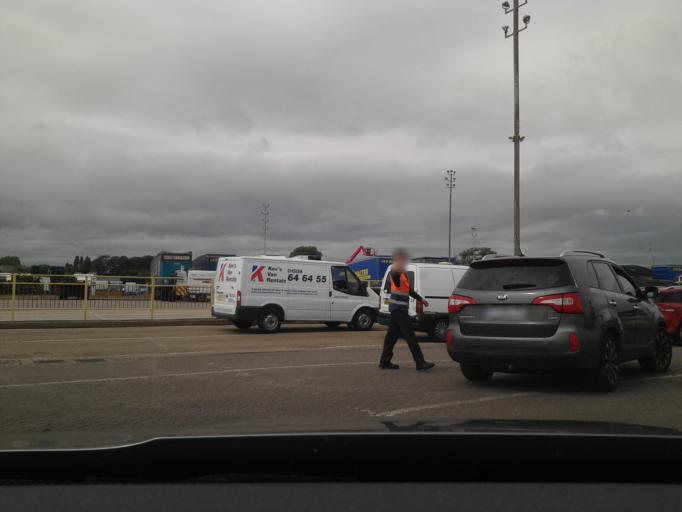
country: GB
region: England
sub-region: Portsmouth
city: Portsmouth
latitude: 50.8122
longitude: -1.0928
